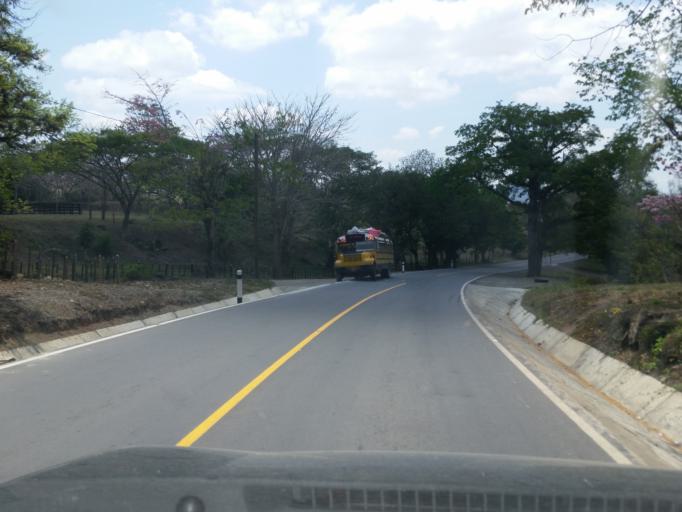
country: NI
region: Boaco
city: Boaco
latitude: 12.5308
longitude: -85.5661
